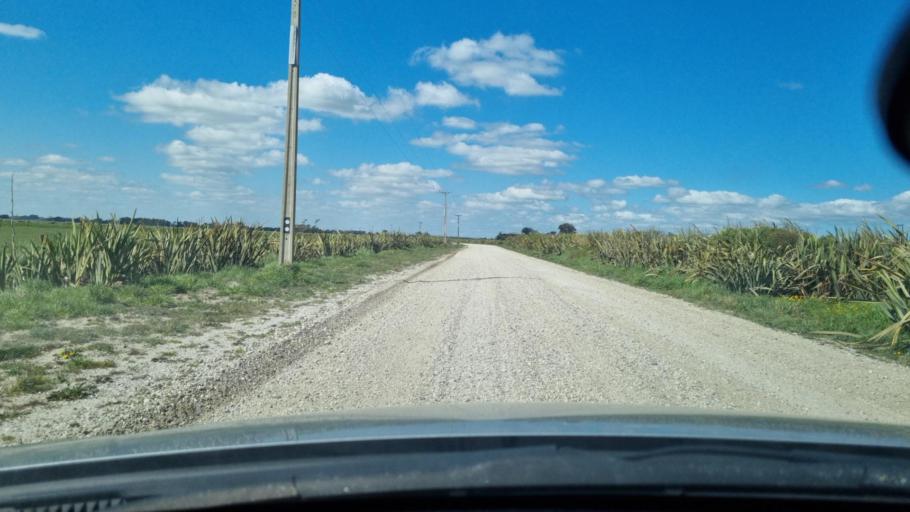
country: NZ
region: Southland
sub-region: Invercargill City
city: Invercargill
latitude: -46.3933
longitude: 168.2439
